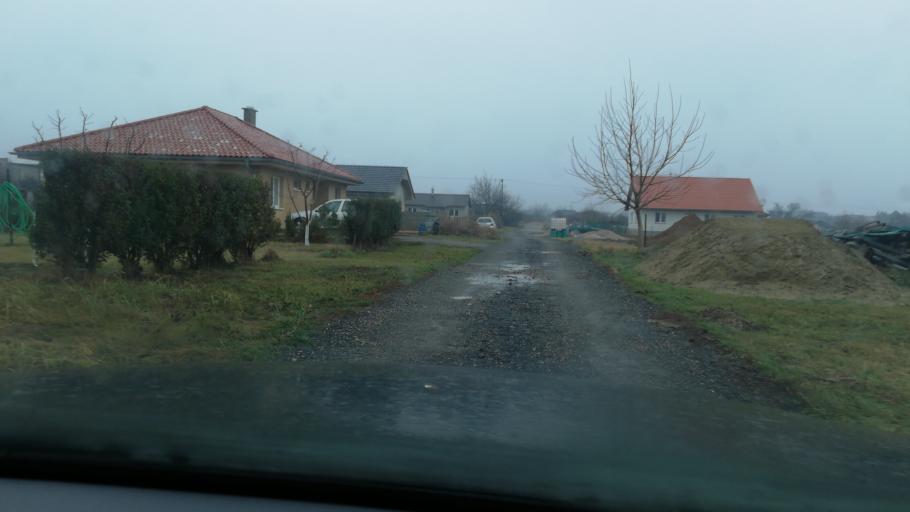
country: SK
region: Nitriansky
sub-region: Okres Nitra
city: Nitra
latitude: 48.3152
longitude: 17.9865
